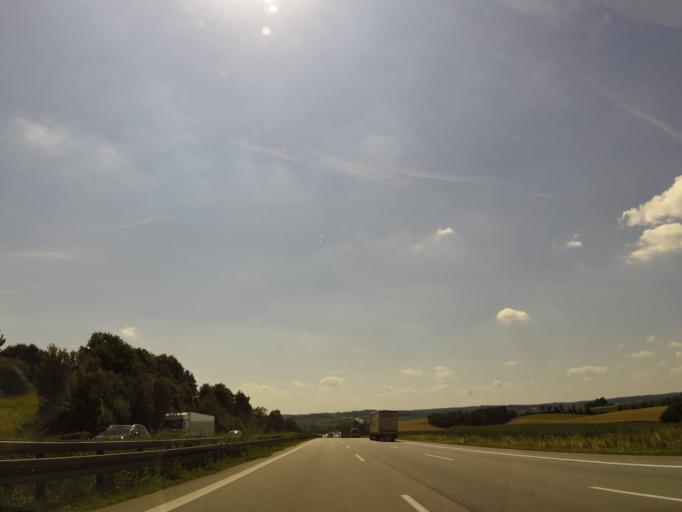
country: DE
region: Bavaria
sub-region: Upper Bavaria
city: Rohrbach
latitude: 48.6048
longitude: 11.5499
